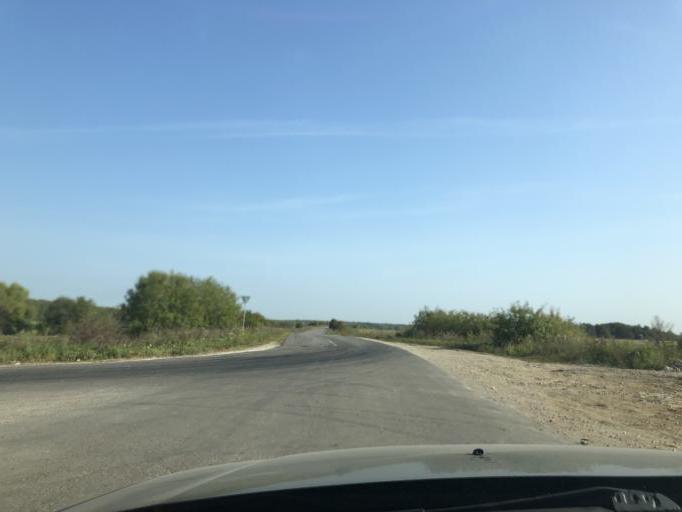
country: RU
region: Tula
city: Novogurovskiy
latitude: 54.4151
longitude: 37.3125
